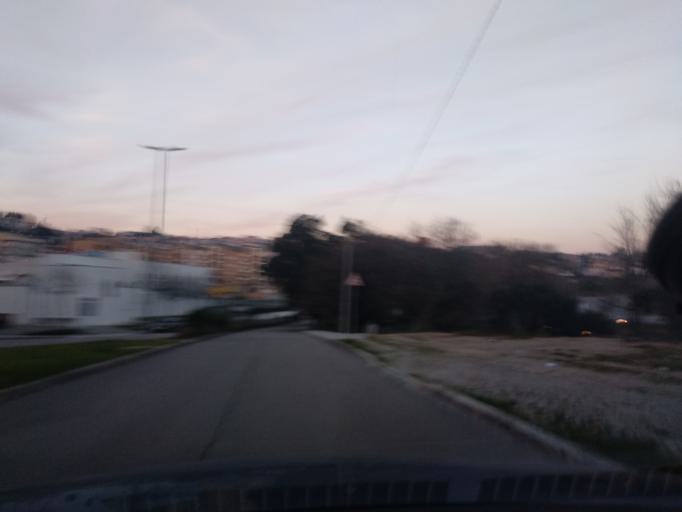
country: PT
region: Porto
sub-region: Paredes
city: Lordelo
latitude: 41.2357
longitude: -8.4134
